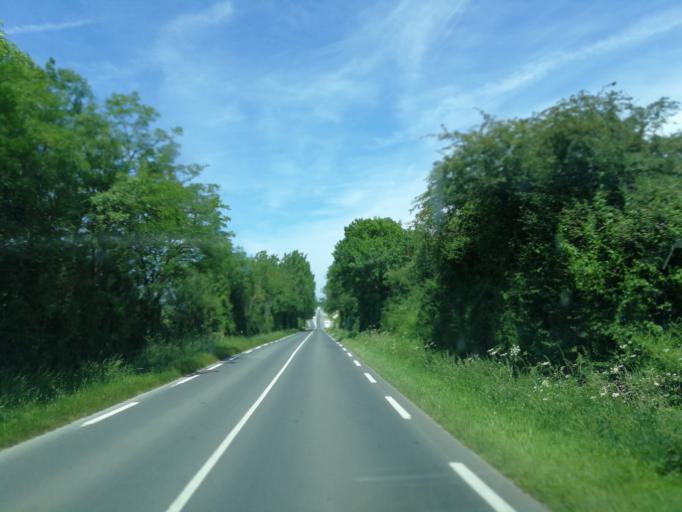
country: FR
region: Pays de la Loire
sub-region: Departement de la Vendee
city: Antigny
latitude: 46.6090
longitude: -0.7866
